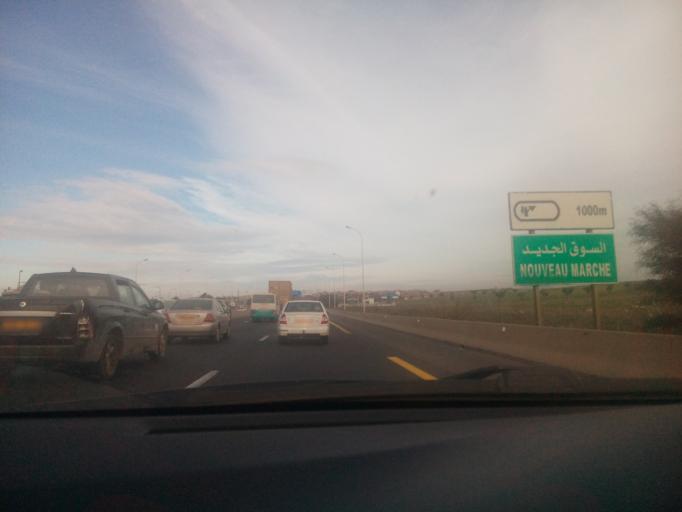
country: DZ
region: Oran
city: Es Senia
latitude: 35.5922
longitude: -0.5720
